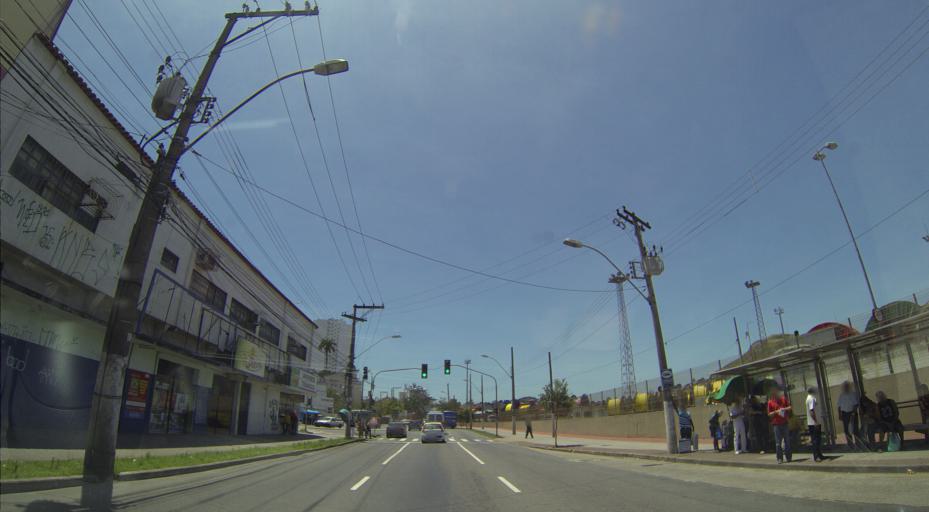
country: BR
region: Espirito Santo
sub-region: Vitoria
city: Vitoria
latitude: -20.3213
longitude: -40.3460
